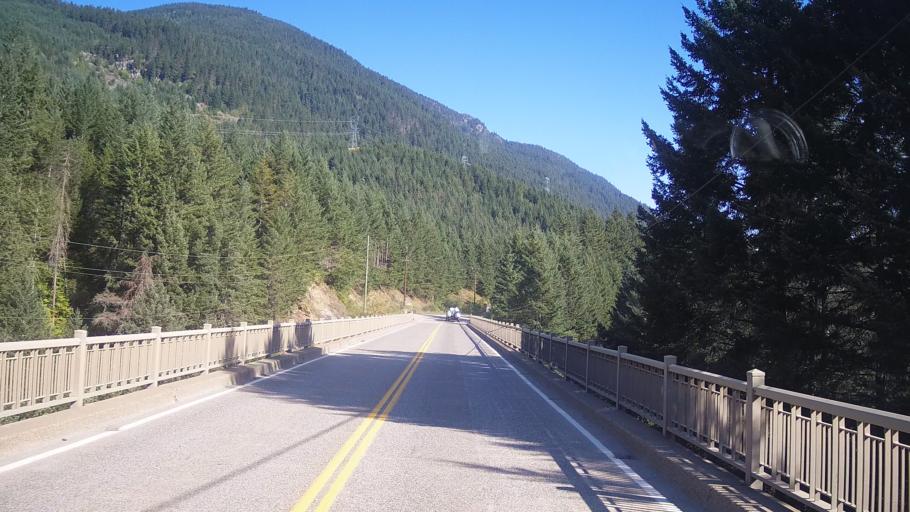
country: CA
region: British Columbia
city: Hope
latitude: 49.6646
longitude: -121.4191
